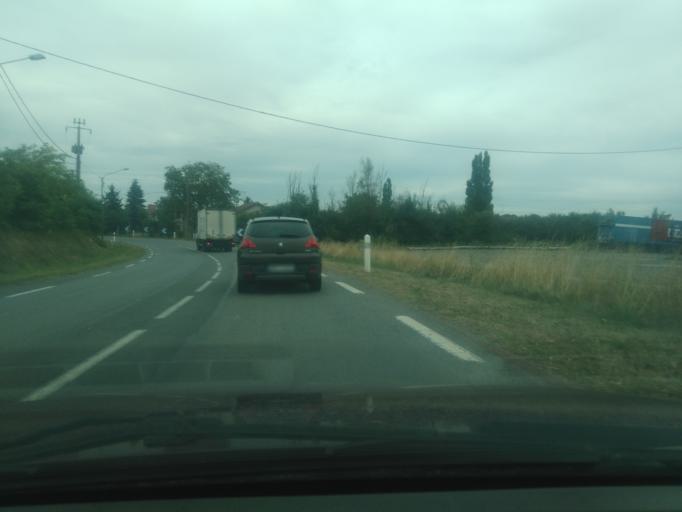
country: FR
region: Poitou-Charentes
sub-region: Departement de la Vienne
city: Saint-Savin
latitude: 46.5609
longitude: 0.8582
